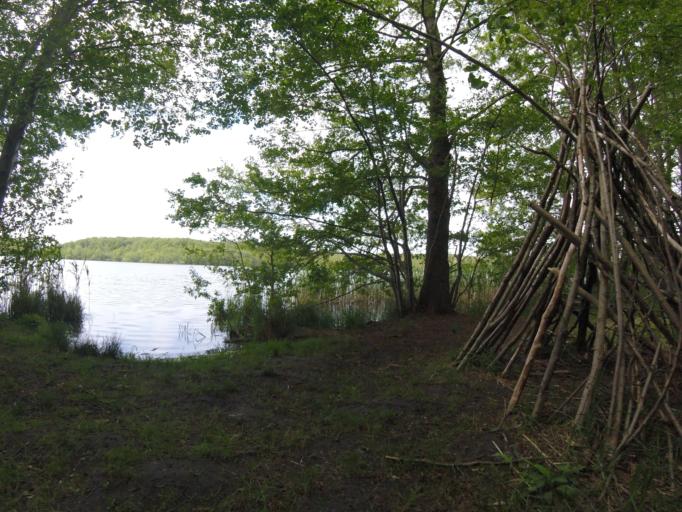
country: DE
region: Brandenburg
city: Bestensee
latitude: 52.2170
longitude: 13.6411
